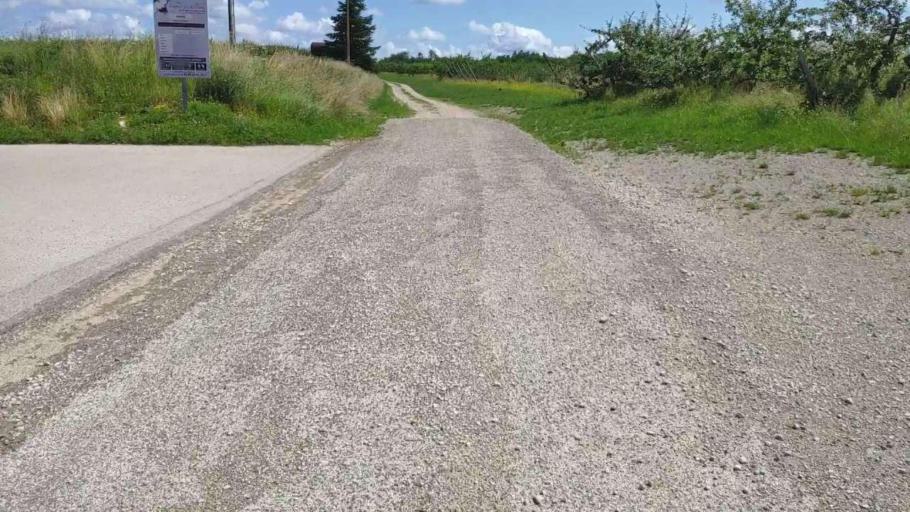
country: FR
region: Franche-Comte
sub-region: Departement du Jura
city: Poligny
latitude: 46.8326
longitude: 5.5679
